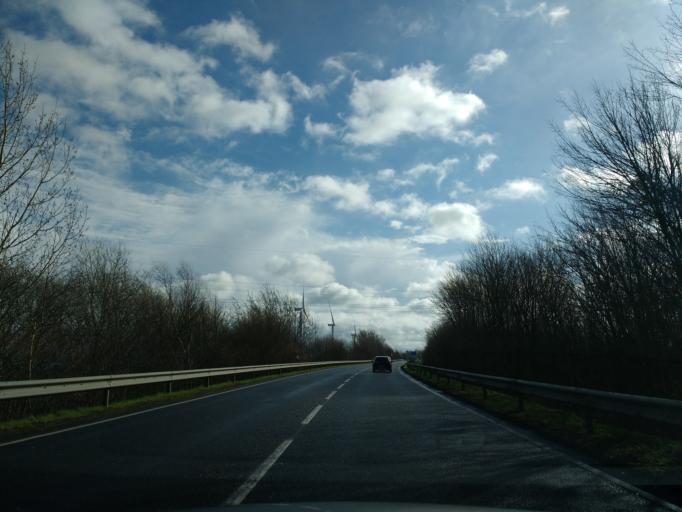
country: DE
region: Lower Saxony
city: Cuxhaven
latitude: 53.8201
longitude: 8.7049
